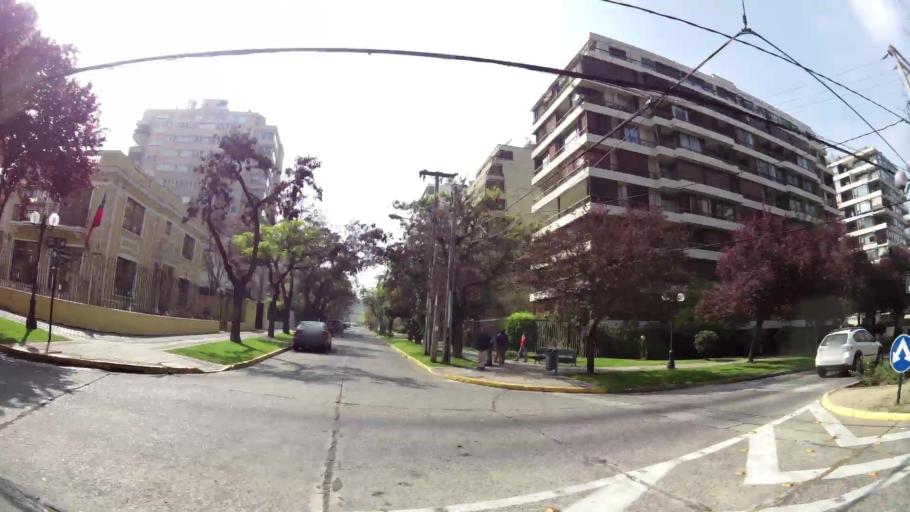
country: CL
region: Santiago Metropolitan
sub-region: Provincia de Santiago
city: Villa Presidente Frei, Nunoa, Santiago, Chile
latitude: -33.4271
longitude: -70.5982
